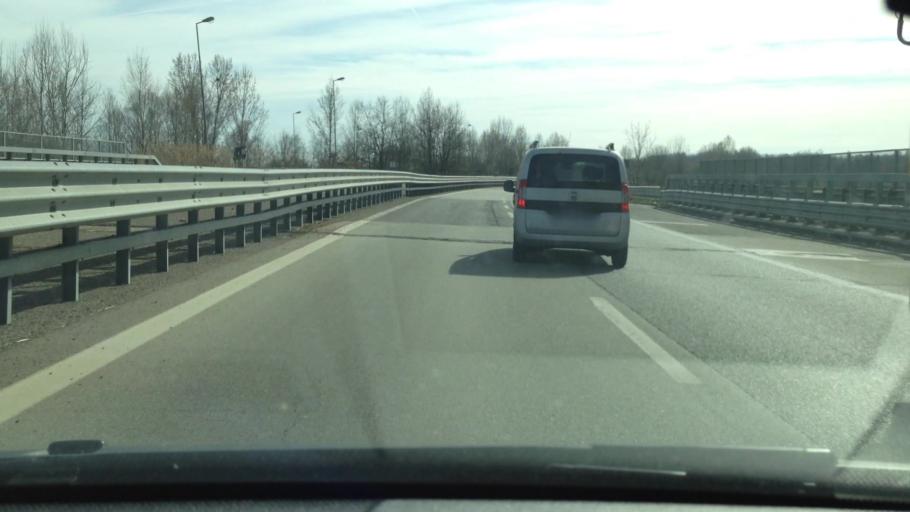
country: IT
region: Piedmont
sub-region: Provincia di Asti
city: Castell'Alfero
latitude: 44.9596
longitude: 8.2284
